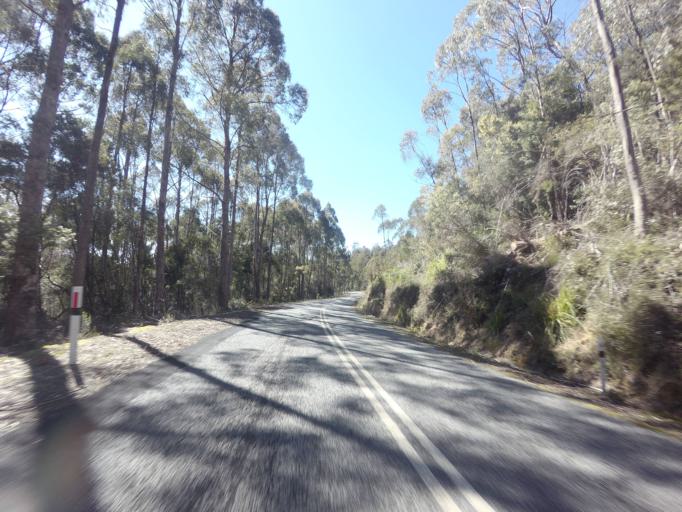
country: AU
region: Tasmania
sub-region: Huon Valley
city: Geeveston
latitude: -42.7834
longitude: 146.3993
